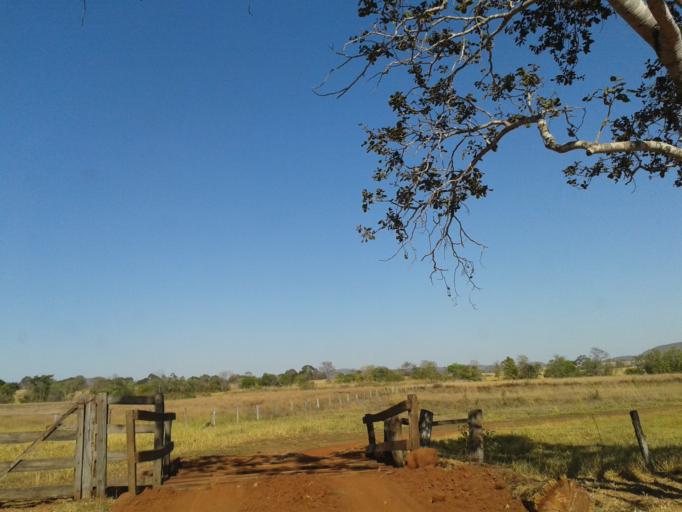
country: BR
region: Minas Gerais
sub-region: Santa Vitoria
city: Santa Vitoria
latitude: -19.1465
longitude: -50.0329
